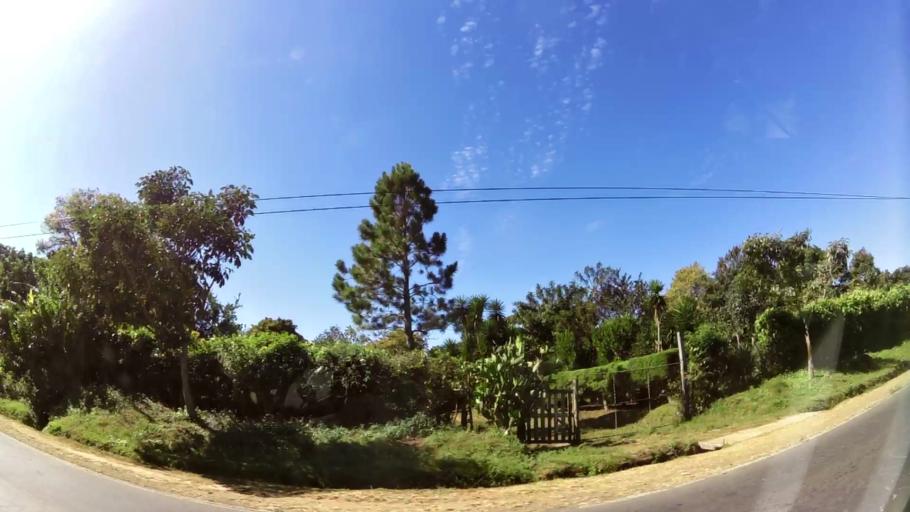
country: SV
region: Ahuachapan
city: Concepcion de Ataco
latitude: 13.8536
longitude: -89.8437
